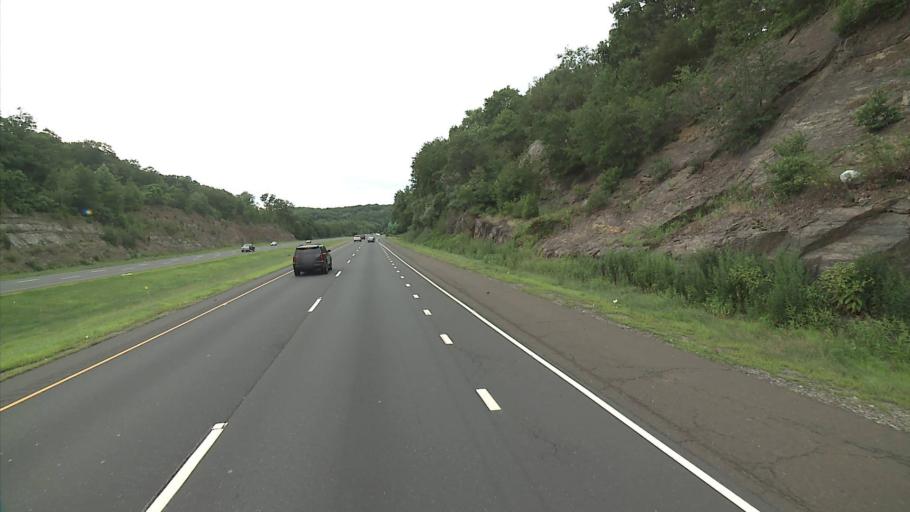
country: US
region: Connecticut
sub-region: Fairfield County
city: Shelton
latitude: 41.2809
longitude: -73.1128
